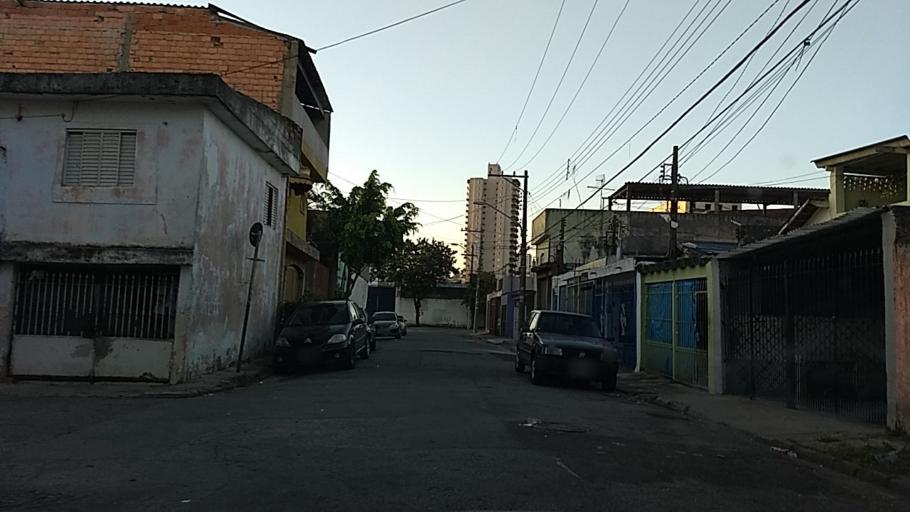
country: BR
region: Sao Paulo
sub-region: Sao Paulo
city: Sao Paulo
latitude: -23.5107
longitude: -46.6050
